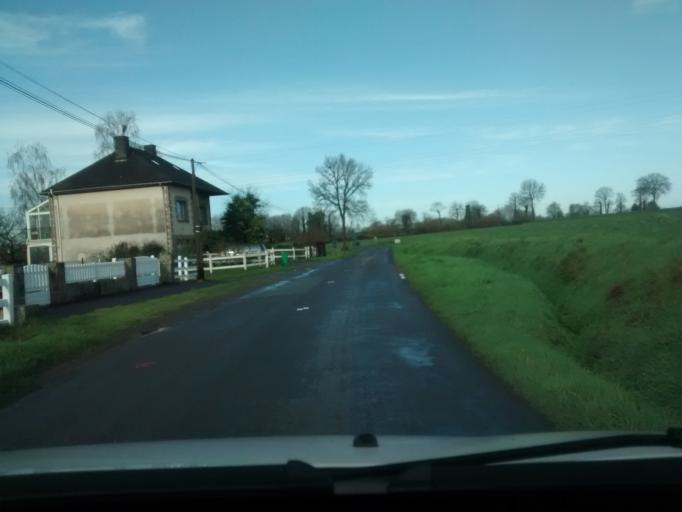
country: FR
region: Brittany
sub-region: Departement d'Ille-et-Vilaine
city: Montgermont
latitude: 48.1391
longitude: -1.7273
